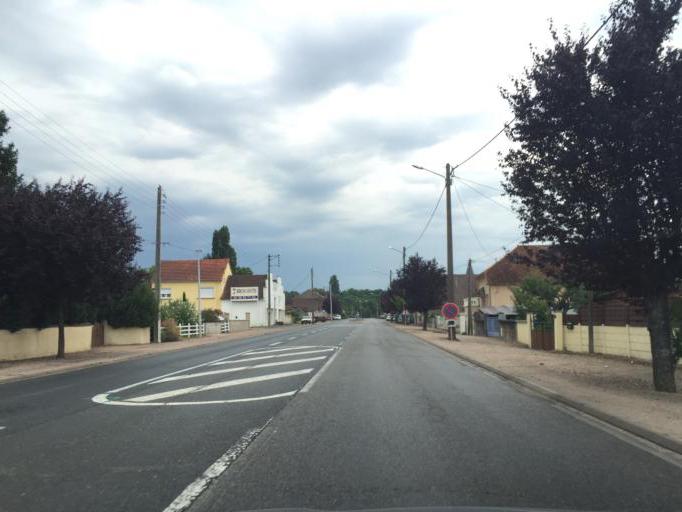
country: FR
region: Auvergne
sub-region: Departement de l'Allier
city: Varennes-sur-Allier
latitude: 46.3530
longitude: 3.3772
